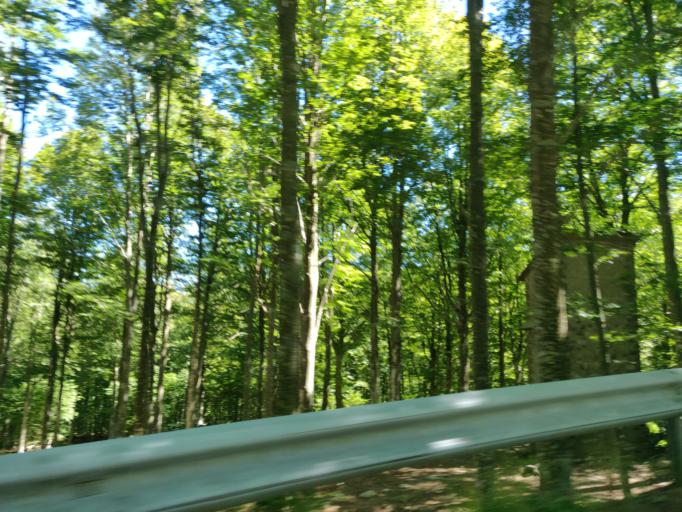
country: IT
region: Tuscany
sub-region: Provincia di Siena
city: Abbadia San Salvatore
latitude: 42.8987
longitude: 11.6317
